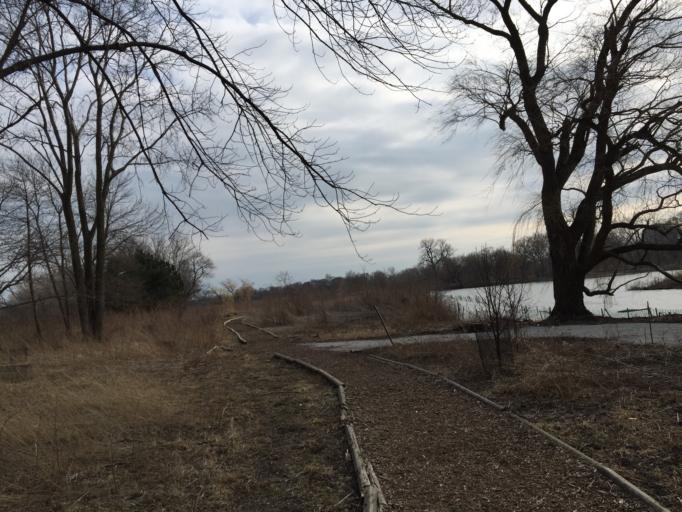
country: US
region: Illinois
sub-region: Cook County
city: Chicago
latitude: 41.7860
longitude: -87.5806
